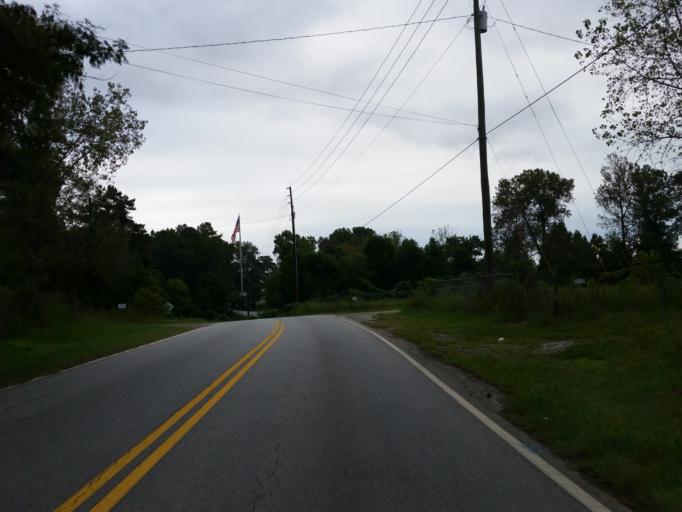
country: US
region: Georgia
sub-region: Cobb County
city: Vinings
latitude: 33.8043
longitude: -84.5014
